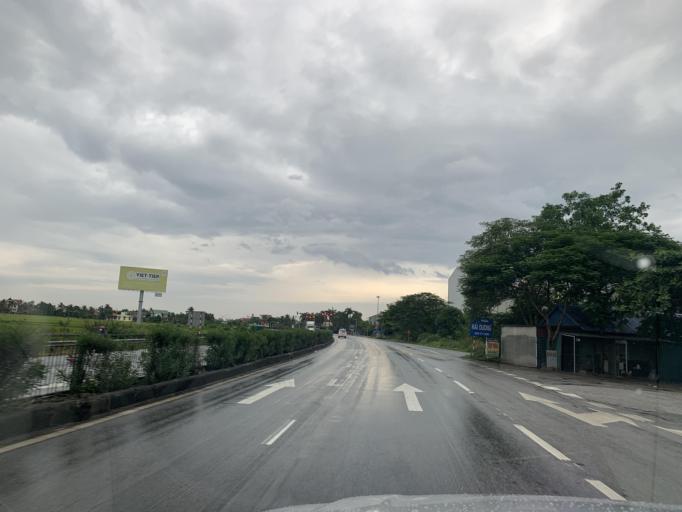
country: VN
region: Hai Duong
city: Phu Thai
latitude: 20.9440
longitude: 106.5437
